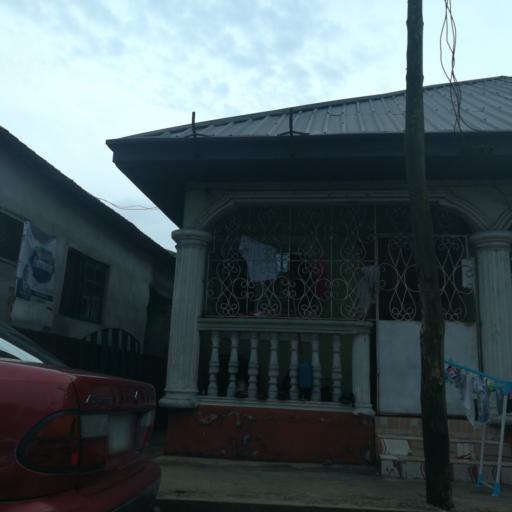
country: NG
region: Rivers
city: Port Harcourt
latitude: 4.7511
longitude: 7.0077
